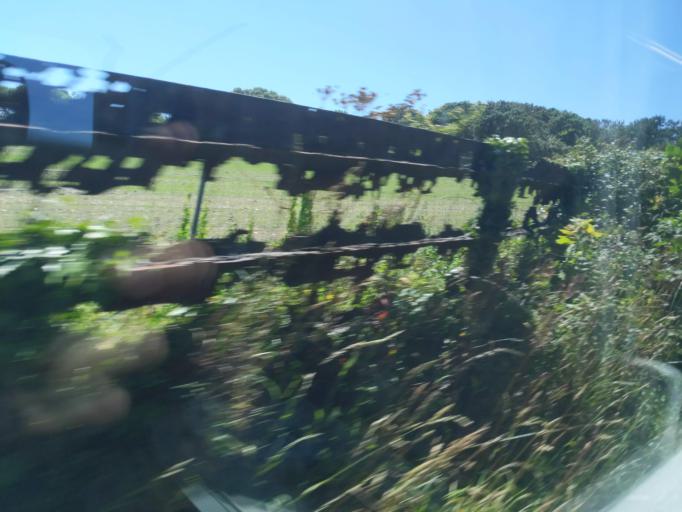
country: GB
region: England
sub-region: Cornwall
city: Chacewater
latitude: 50.2660
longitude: -5.1780
